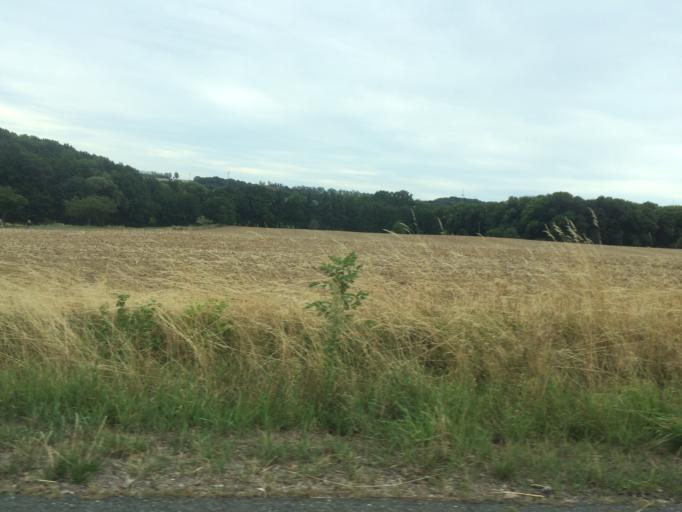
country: DE
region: Saxony
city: Wilsdruff
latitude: 51.0697
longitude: 13.5859
